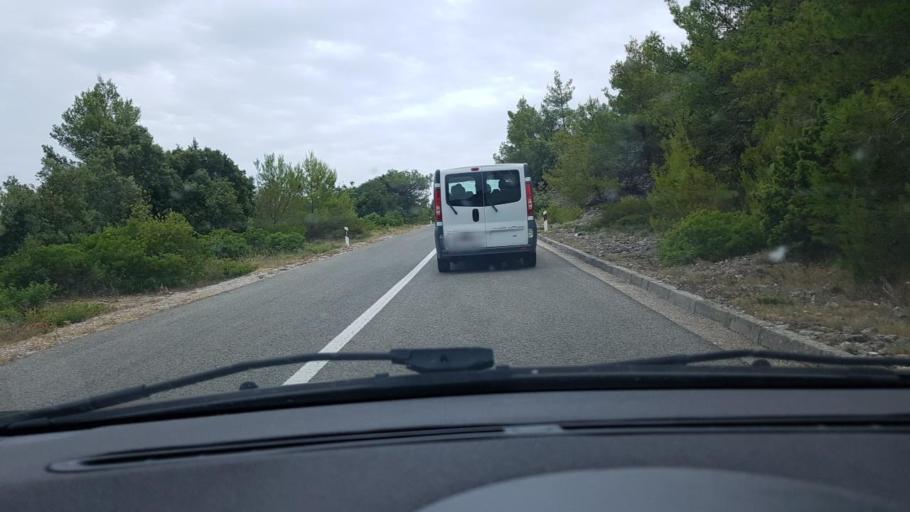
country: HR
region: Dubrovacko-Neretvanska
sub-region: Grad Korcula
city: Zrnovo
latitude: 42.9424
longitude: 17.0246
